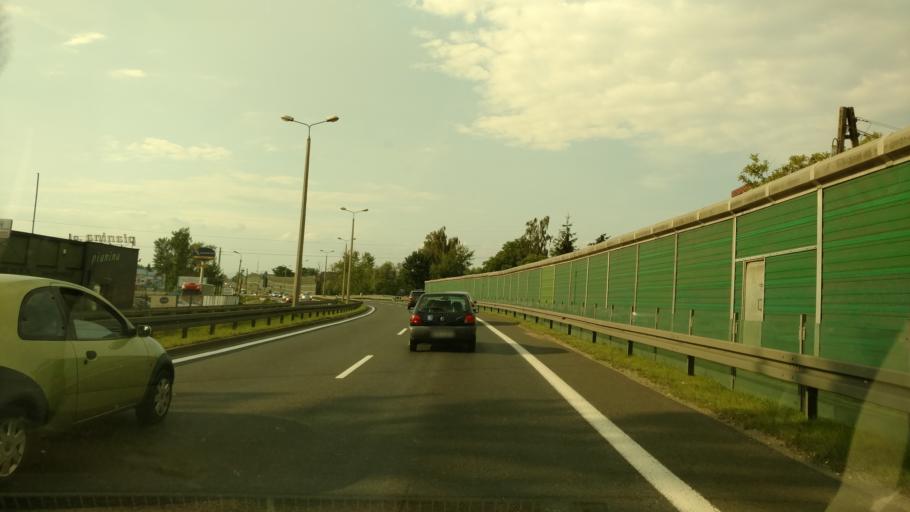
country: PL
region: Silesian Voivodeship
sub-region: Powiat pszczynski
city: Pszczyna
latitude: 49.9795
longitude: 18.9588
